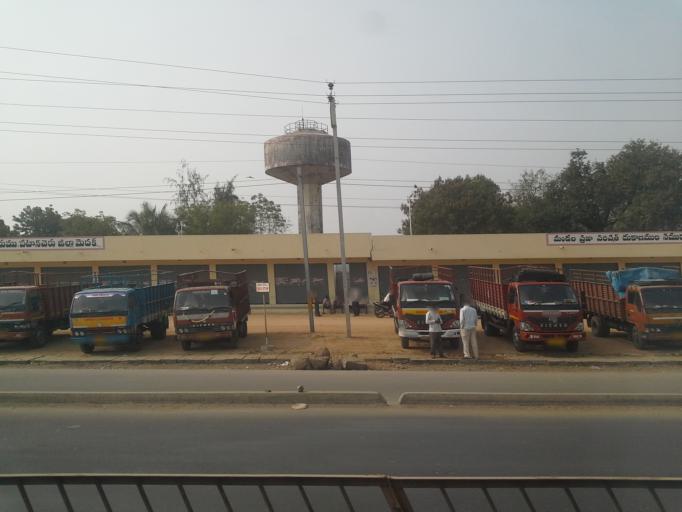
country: IN
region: Telangana
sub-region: Medak
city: Patancheru
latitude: 17.5266
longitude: 78.2694
